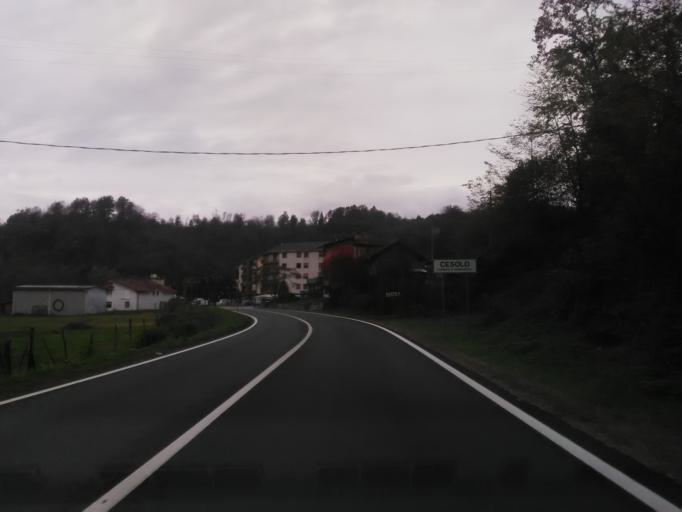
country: IT
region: Piedmont
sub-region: Provincia di Vercelli
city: Valduggia
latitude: 45.7198
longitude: 8.3056
